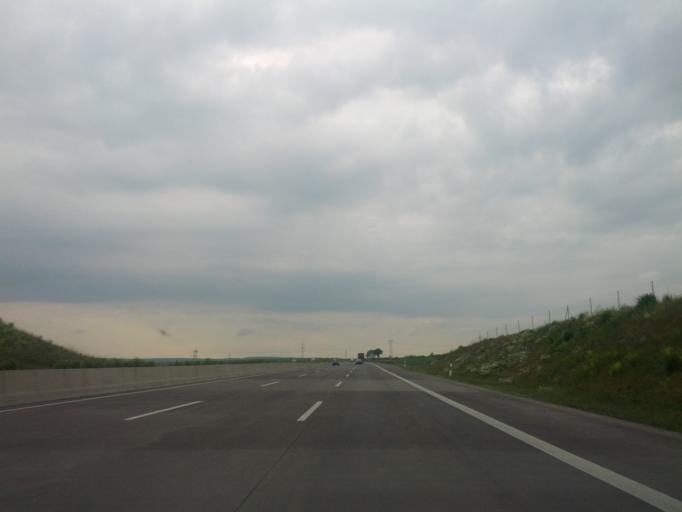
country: DE
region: Thuringia
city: Mechterstadt
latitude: 50.9606
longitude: 10.4878
